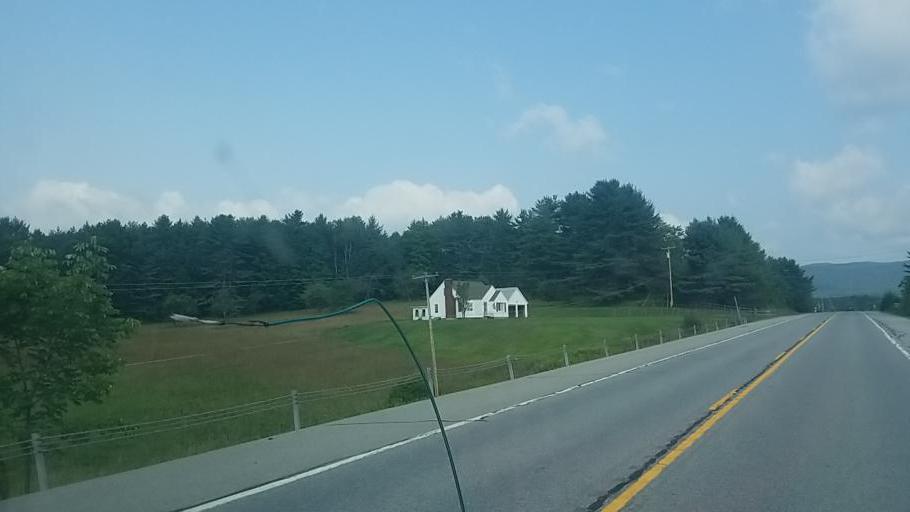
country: US
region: New York
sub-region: Fulton County
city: Gloversville
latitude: 43.0904
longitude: -74.2742
